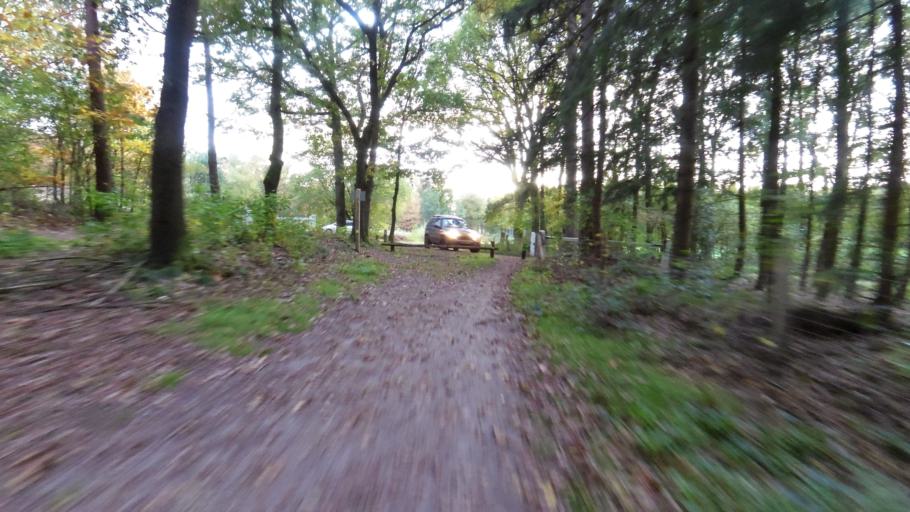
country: NL
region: Gelderland
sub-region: Gemeente Ede
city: Lunteren
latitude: 52.0937
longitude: 5.6682
